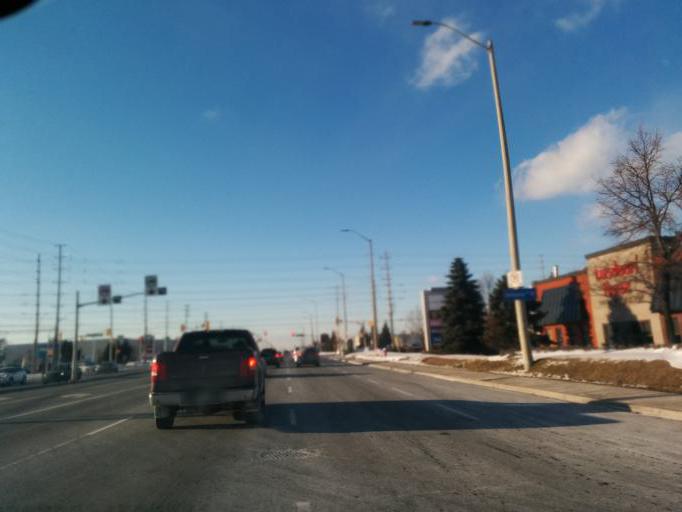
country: CA
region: Ontario
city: Mississauga
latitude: 43.6113
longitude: -79.6944
